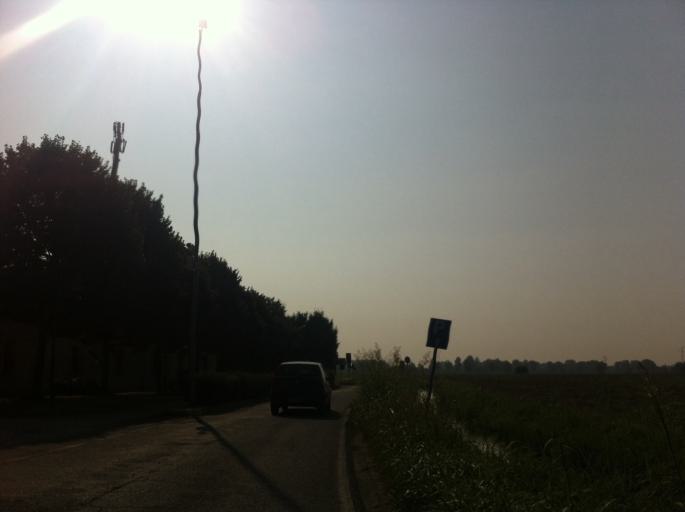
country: IT
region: Lombardy
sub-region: Provincia di Lodi
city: Casalmaiocco
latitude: 45.3521
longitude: 9.3783
